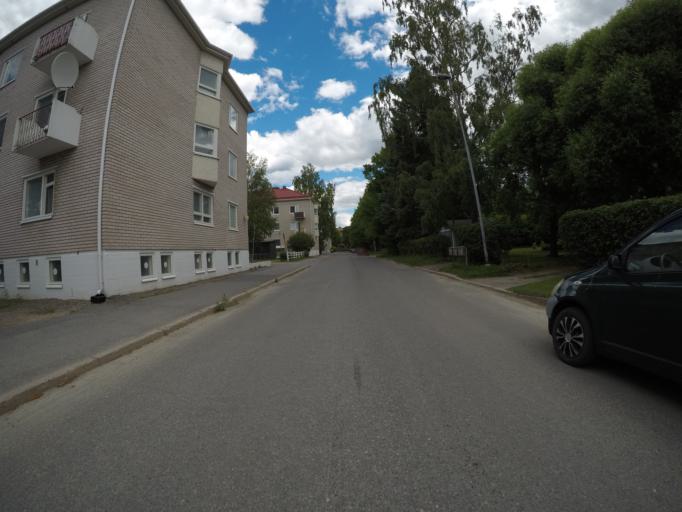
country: FI
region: Haeme
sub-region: Haemeenlinna
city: Haemeenlinna
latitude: 60.9957
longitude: 24.4428
